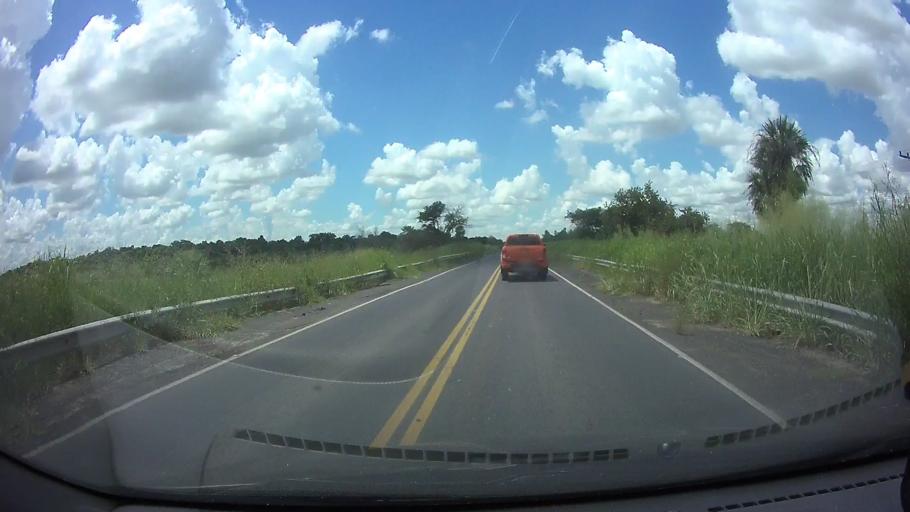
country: PY
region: Presidente Hayes
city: Nanawa
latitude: -25.2018
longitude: -57.6437
